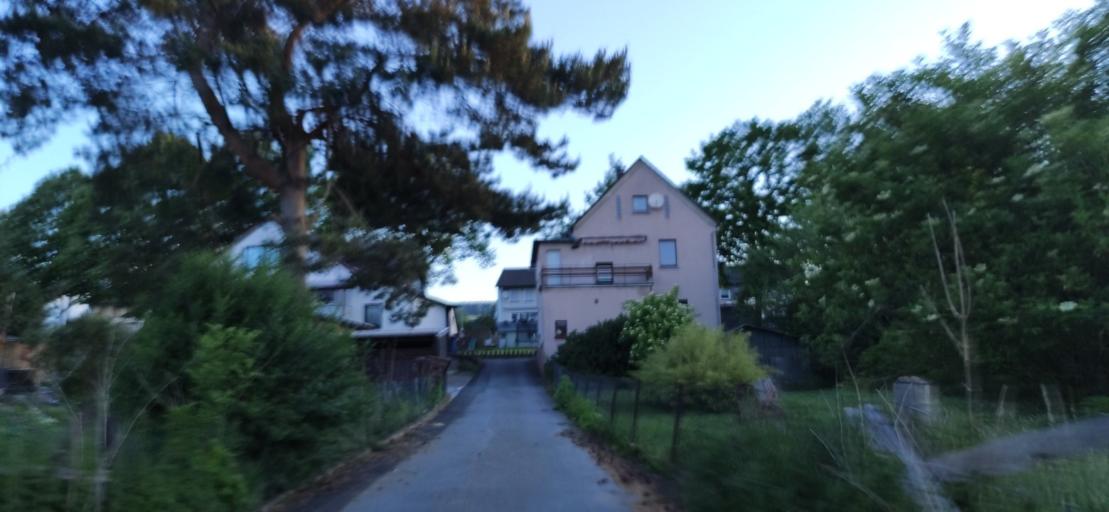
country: DE
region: North Rhine-Westphalia
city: Beverungen
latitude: 51.7083
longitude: 9.3101
